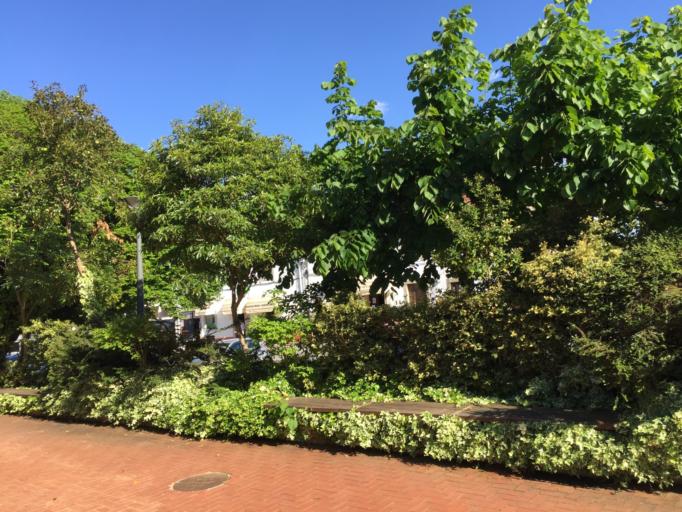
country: PT
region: Leiria
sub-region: Pedrogao Grande
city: Pedrogao Grande
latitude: 39.9184
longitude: -8.1451
